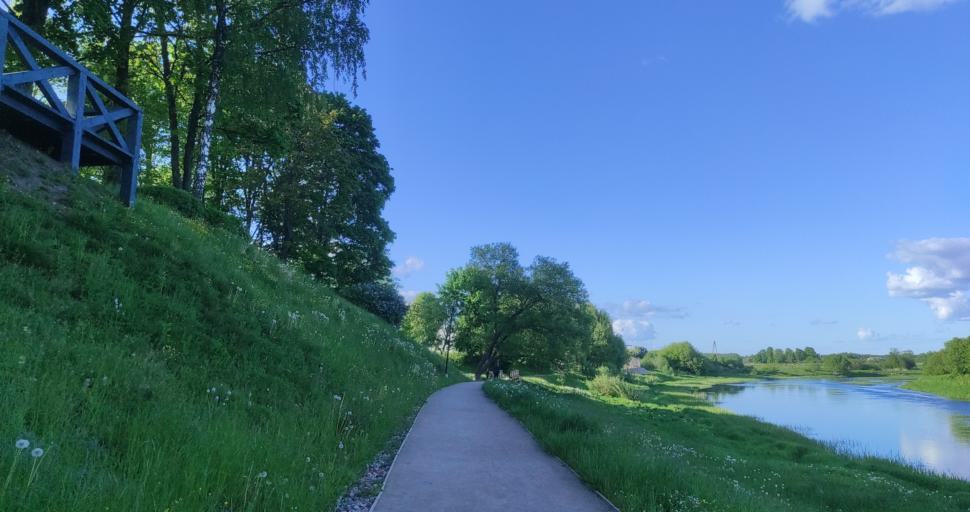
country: LV
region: Skrunda
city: Skrunda
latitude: 56.6741
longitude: 22.0262
